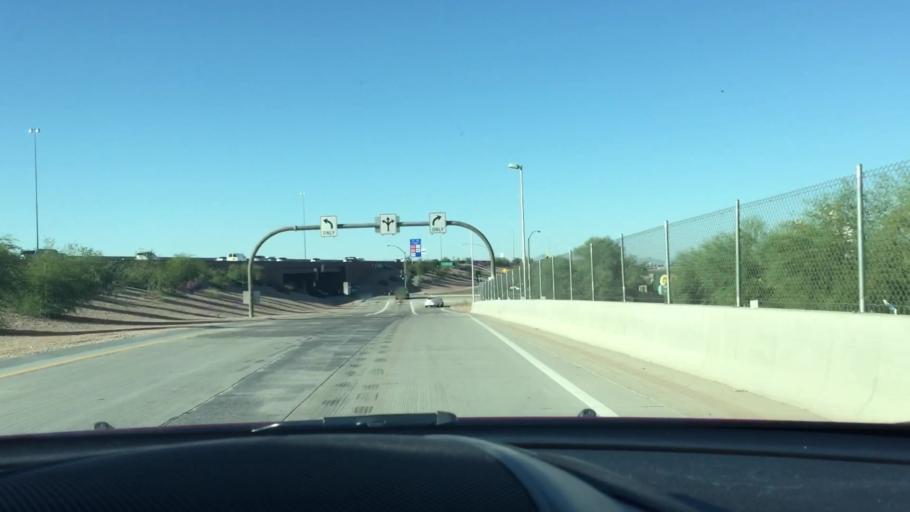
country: US
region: Arizona
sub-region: Maricopa County
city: Mesa
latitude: 33.4467
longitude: -111.8549
